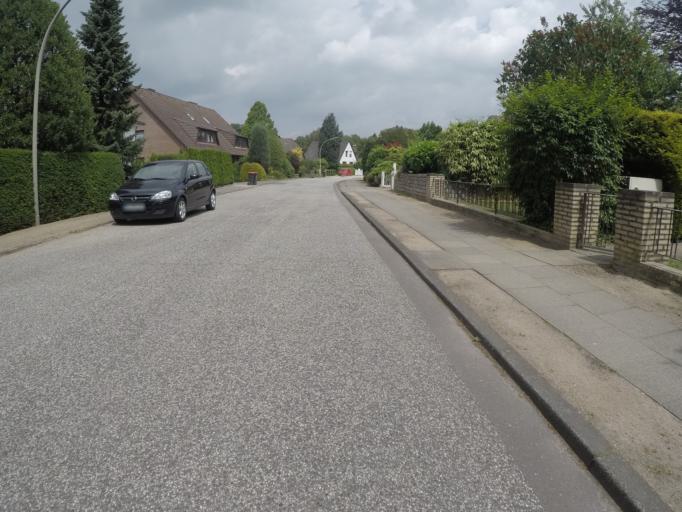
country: DE
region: Hamburg
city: Langenhorn
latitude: 53.6409
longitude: 9.9668
